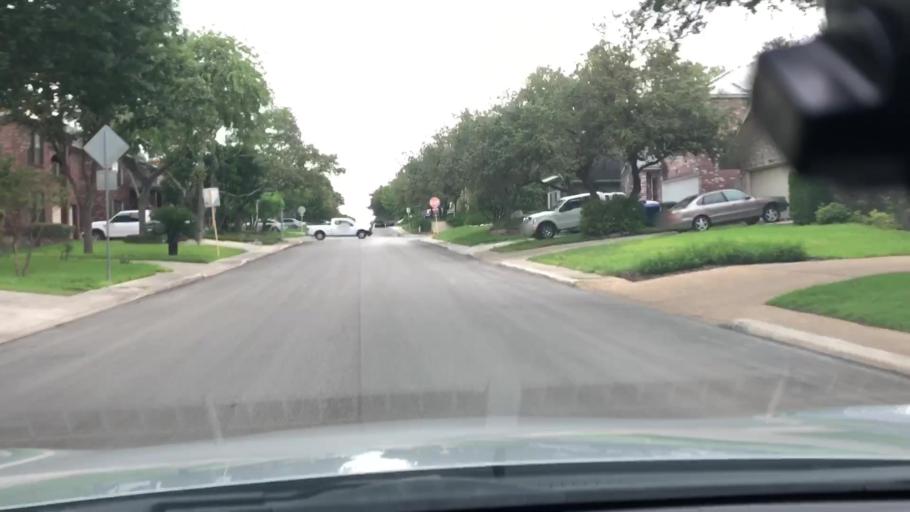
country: US
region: Texas
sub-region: Bexar County
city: Leon Valley
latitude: 29.5000
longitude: -98.6682
